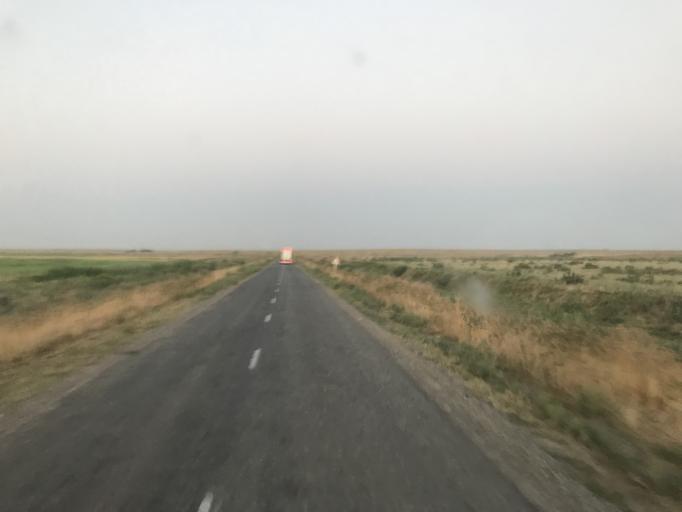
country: UZ
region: Toshkent
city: Chinoz
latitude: 41.2018
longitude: 68.5975
